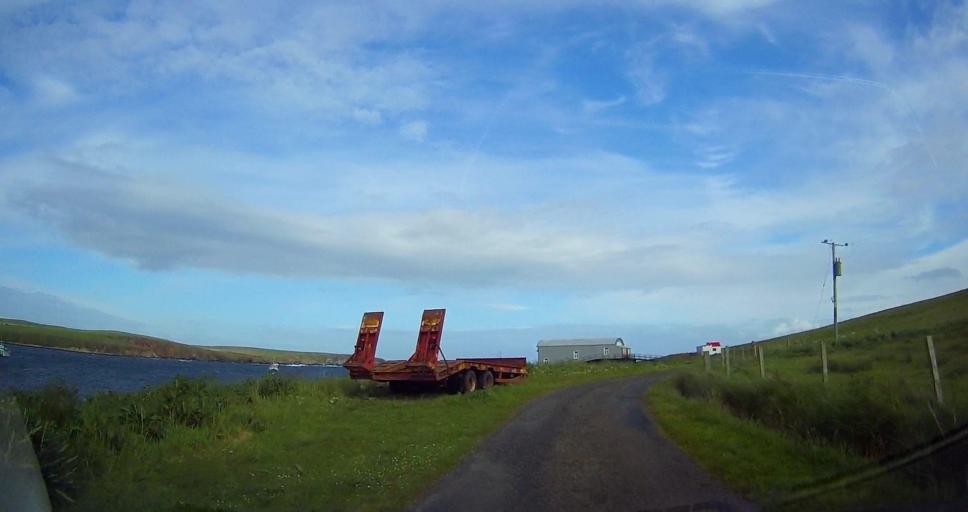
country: GB
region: Scotland
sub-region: Orkney Islands
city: Stromness
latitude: 58.7804
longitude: -3.2304
